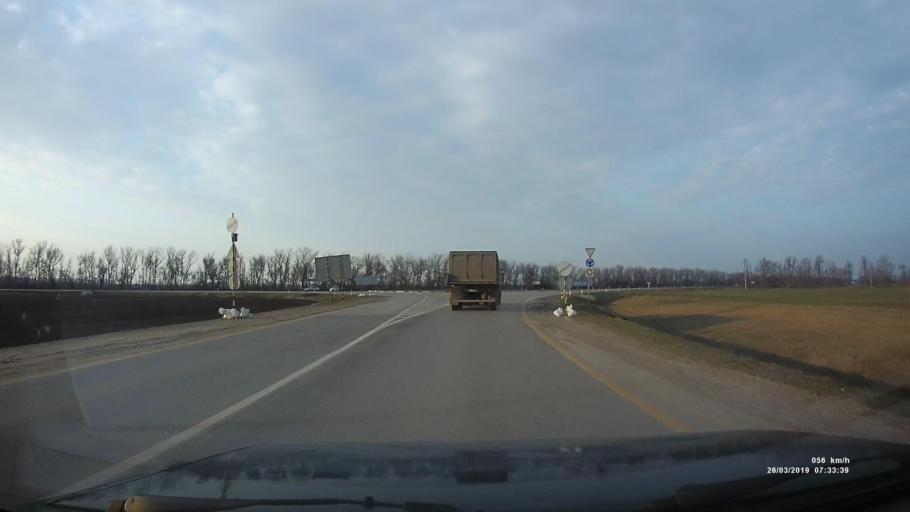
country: RU
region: Rostov
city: Novobessergenovka
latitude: 47.2133
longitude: 38.7690
